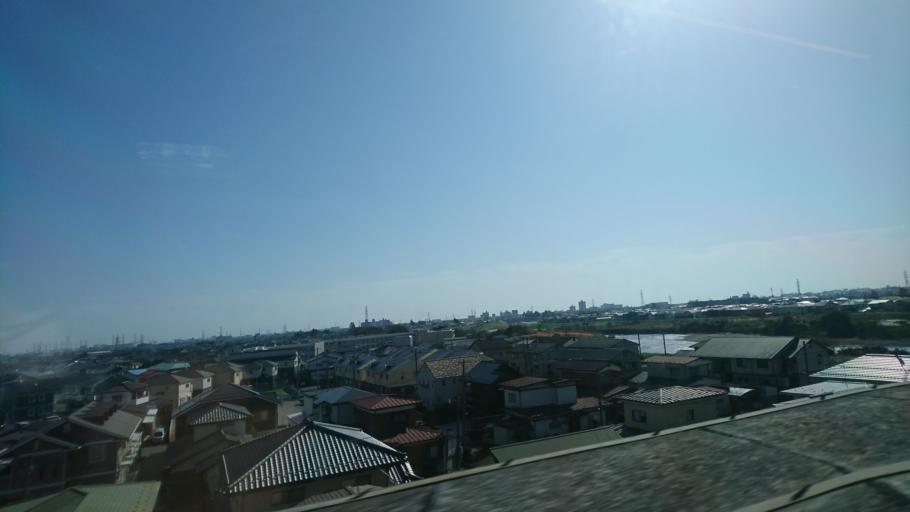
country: JP
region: Miyagi
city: Rifu
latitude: 38.2994
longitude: 140.9554
